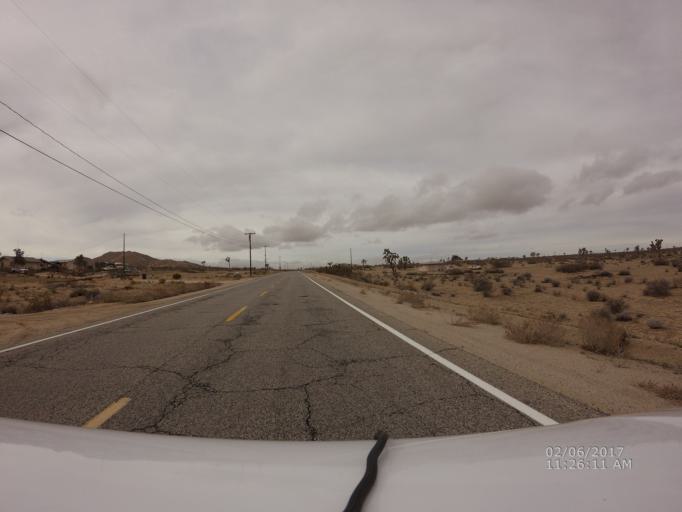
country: US
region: California
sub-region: Los Angeles County
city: Lake Los Angeles
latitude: 34.6904
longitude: -117.7696
